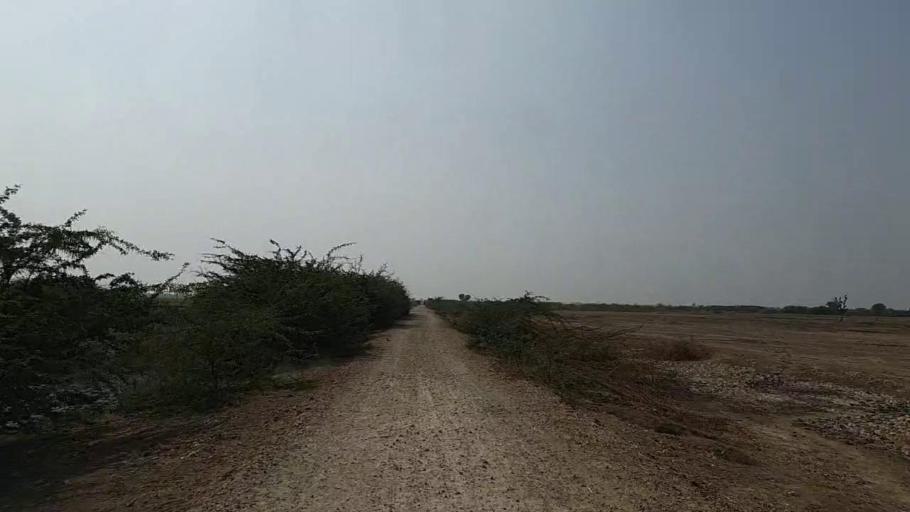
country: PK
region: Sindh
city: Naukot
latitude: 24.7606
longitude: 69.3153
